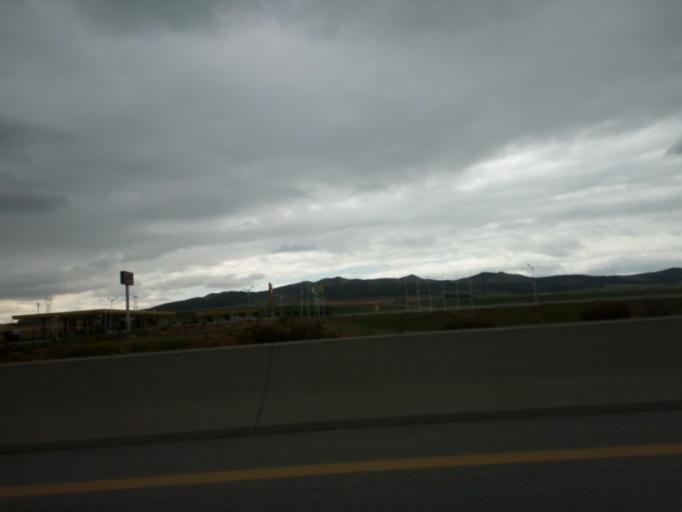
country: DZ
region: Mila
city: Chelghoum el Aid
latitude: 36.1817
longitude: 6.2490
